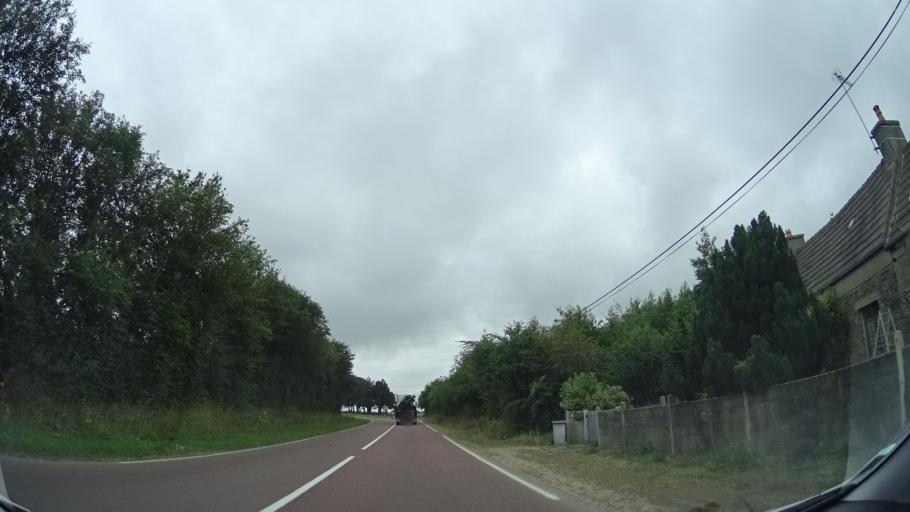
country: FR
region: Lower Normandy
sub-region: Departement de la Manche
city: Portbail
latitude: 49.3528
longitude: -1.6719
